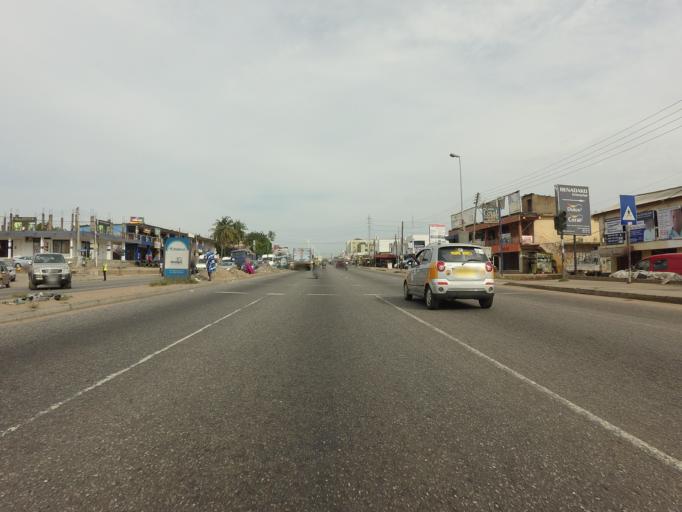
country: GH
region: Greater Accra
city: Dome
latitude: 5.6218
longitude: -0.2315
